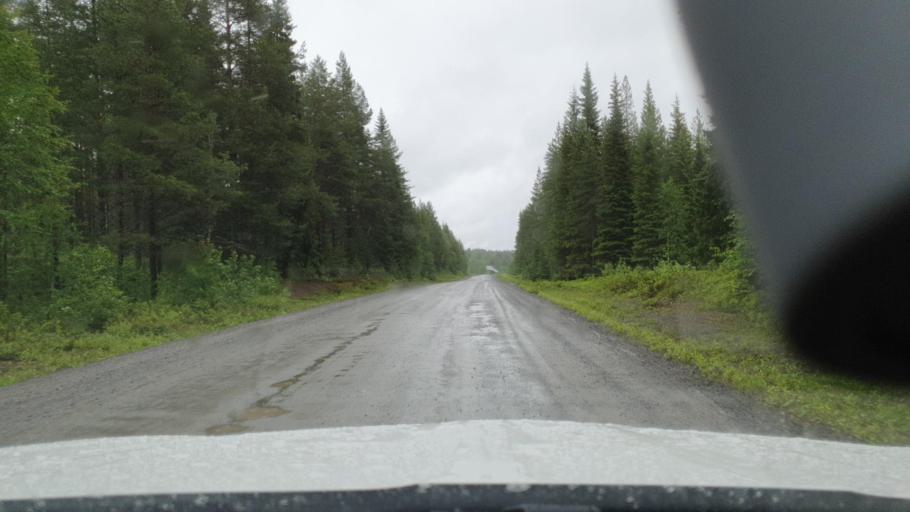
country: SE
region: Vaesterbotten
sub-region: Skelleftea Kommun
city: Burtraesk
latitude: 64.3846
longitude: 20.2994
